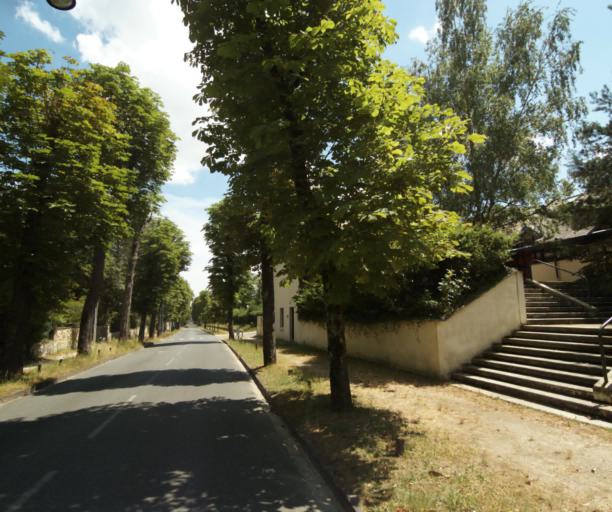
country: FR
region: Ile-de-France
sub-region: Departement de Seine-et-Marne
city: Samois-sur-Seine
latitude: 48.4530
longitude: 2.7429
